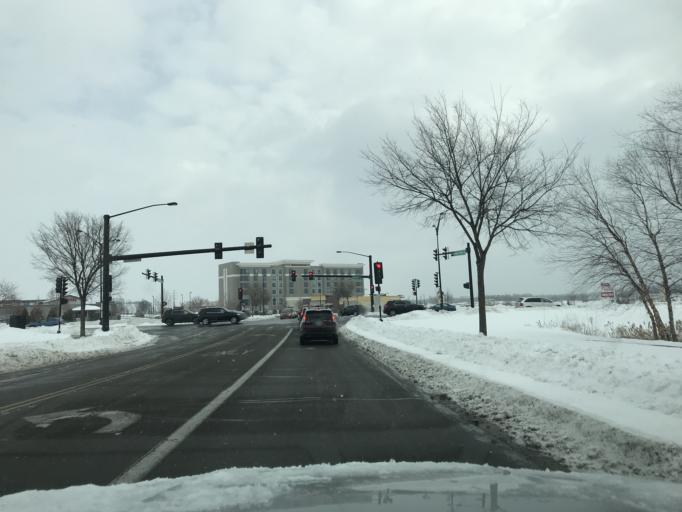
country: US
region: Wisconsin
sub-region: Dane County
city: Sun Prairie
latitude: 43.1665
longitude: -89.2733
